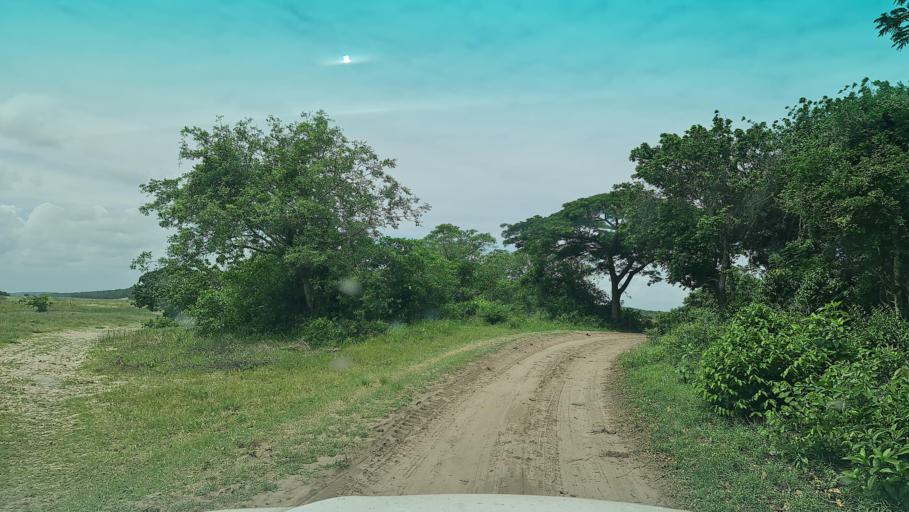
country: MZ
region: Maputo
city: Manhica
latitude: -25.5185
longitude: 32.8661
